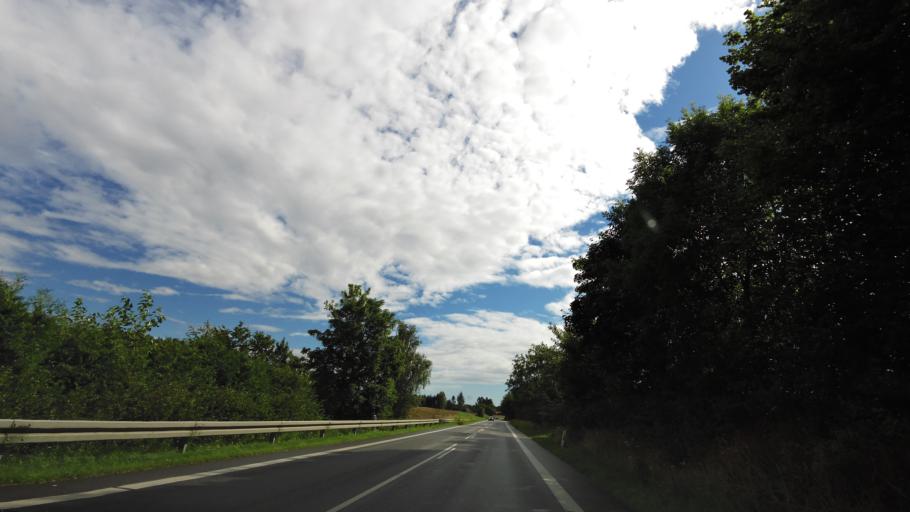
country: DK
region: South Denmark
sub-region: Assens Kommune
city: Vissenbjerg
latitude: 55.4175
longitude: 10.1765
